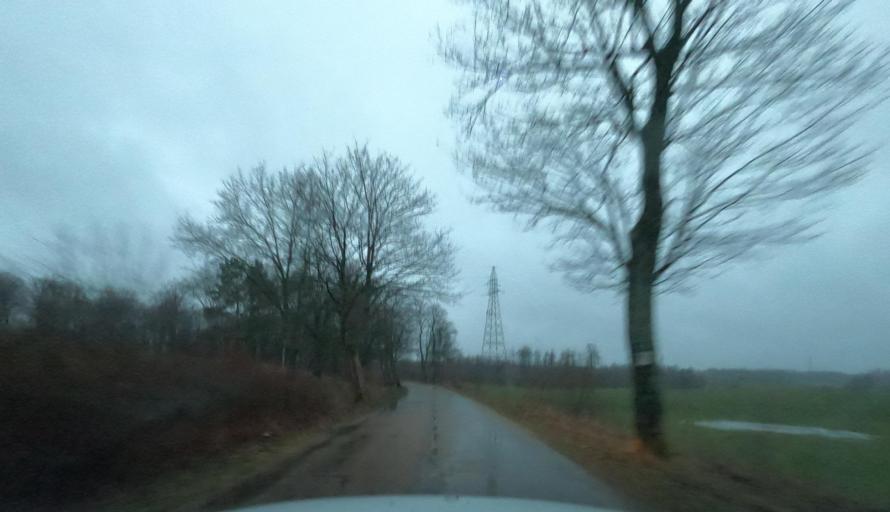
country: PL
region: West Pomeranian Voivodeship
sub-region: Powiat szczecinecki
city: Borne Sulinowo
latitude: 53.6604
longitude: 16.4868
